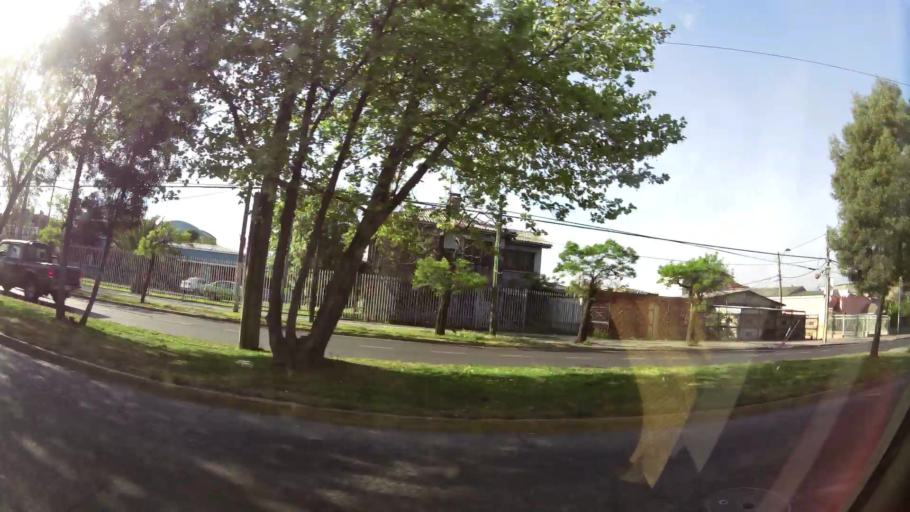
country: CL
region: Santiago Metropolitan
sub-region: Provincia de Santiago
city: Santiago
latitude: -33.5071
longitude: -70.6319
